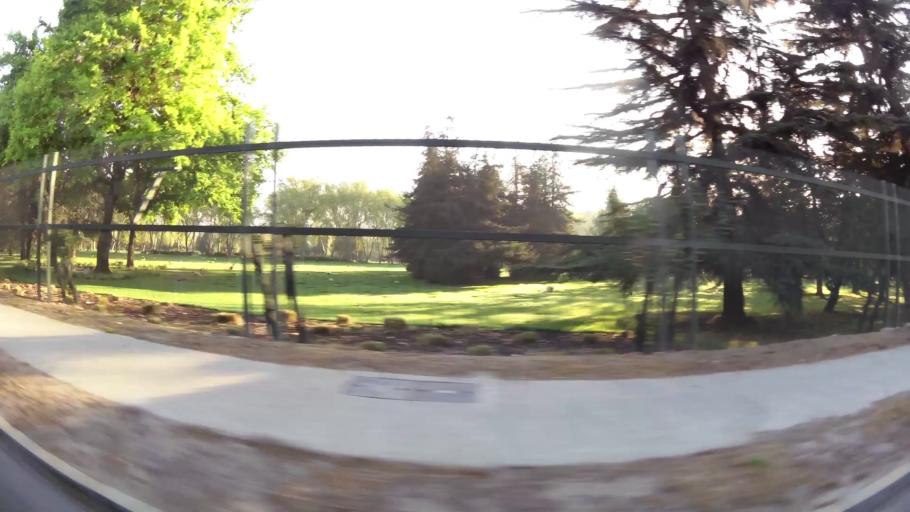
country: CL
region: Santiago Metropolitan
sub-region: Provincia de Santiago
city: Santiago
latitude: -33.3867
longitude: -70.6352
